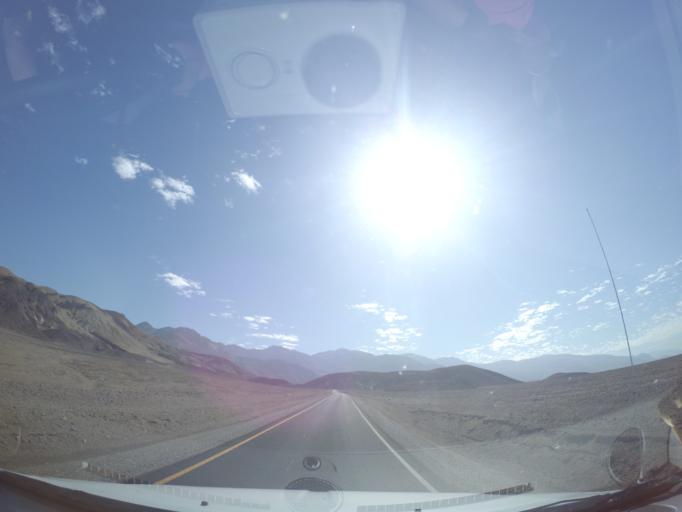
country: US
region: Nevada
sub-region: Nye County
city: Beatty
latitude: 36.3338
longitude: -116.8218
